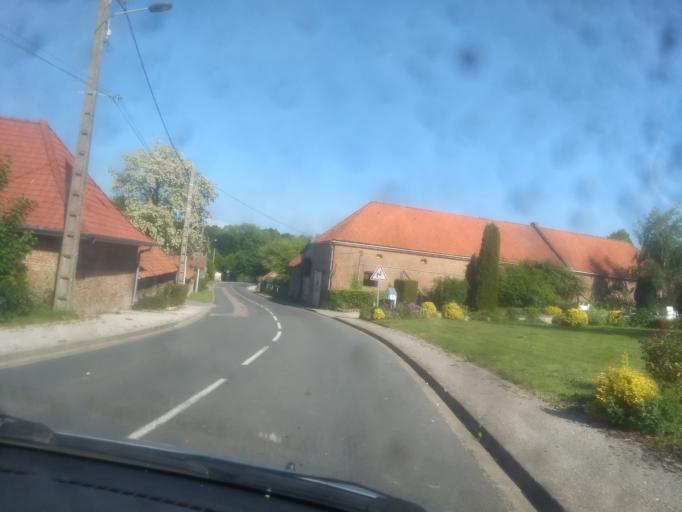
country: FR
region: Picardie
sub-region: Departement de la Somme
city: Crecy-en-Ponthieu
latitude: 50.1710
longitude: 1.8734
